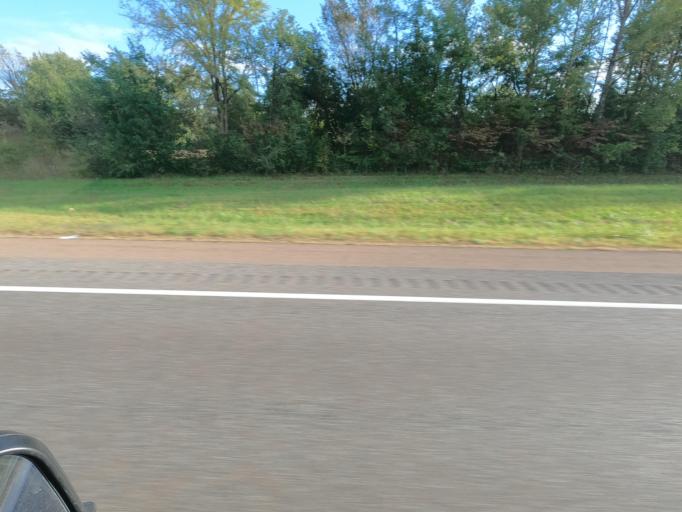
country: US
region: Tennessee
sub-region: Henderson County
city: Lexington
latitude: 35.7696
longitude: -88.4516
